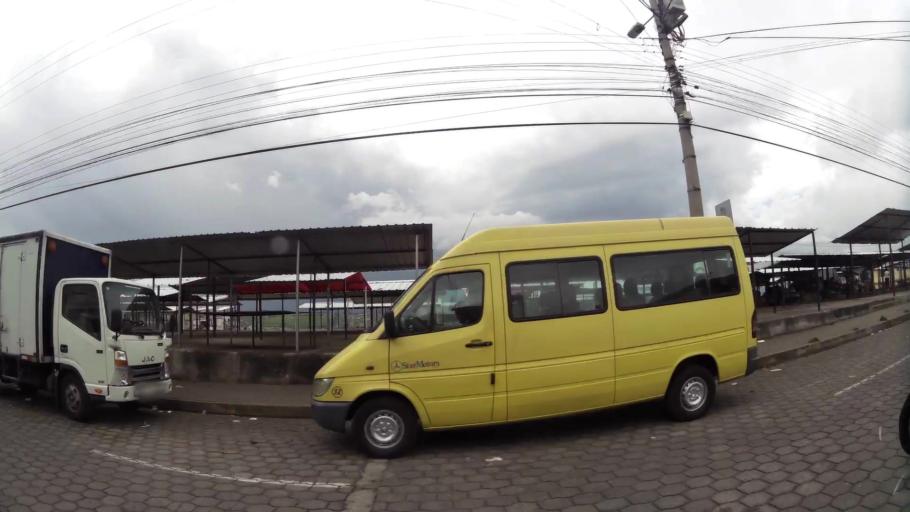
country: EC
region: Pichincha
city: Sangolqui
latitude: -0.3318
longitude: -78.5528
